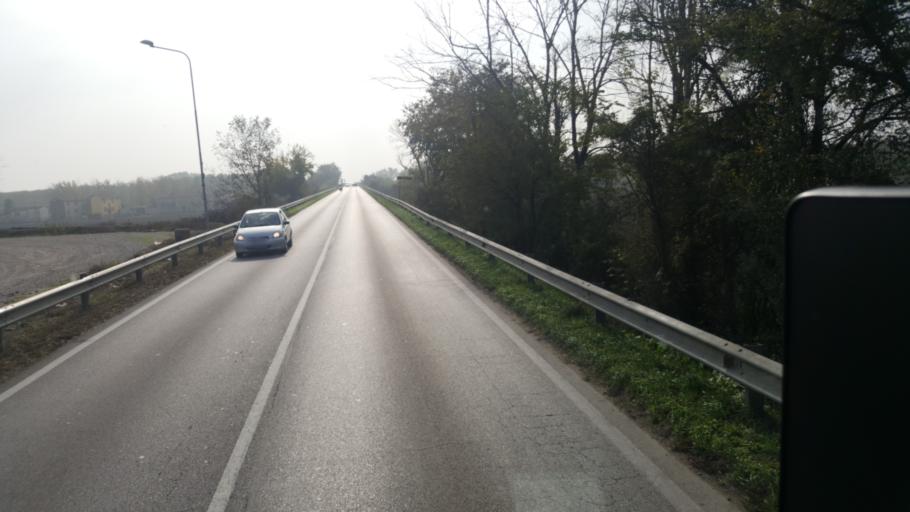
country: IT
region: Lombardy
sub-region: Provincia di Mantova
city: Borgoforte
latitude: 45.0530
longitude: 10.7545
